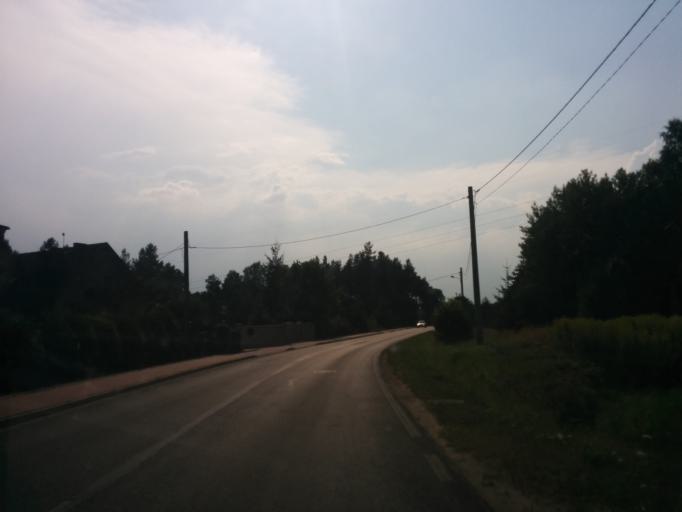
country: PL
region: Silesian Voivodeship
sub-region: Powiat myszkowski
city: Poraj
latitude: 50.6816
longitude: 19.2365
